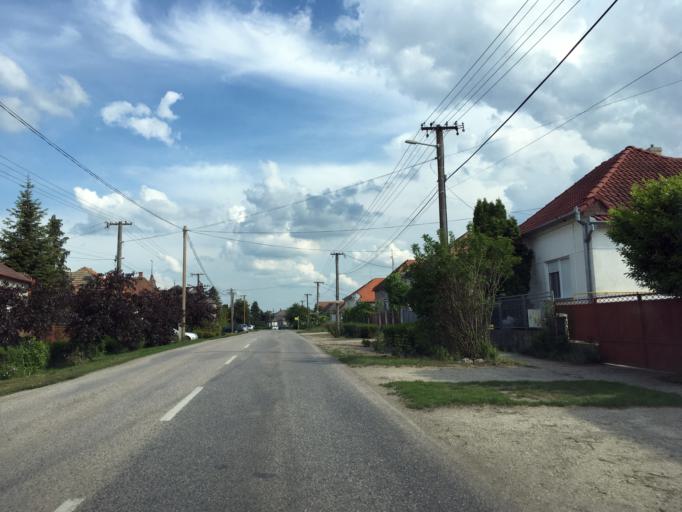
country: SK
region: Nitriansky
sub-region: Okres Komarno
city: Hurbanovo
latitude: 47.8040
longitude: 18.2332
